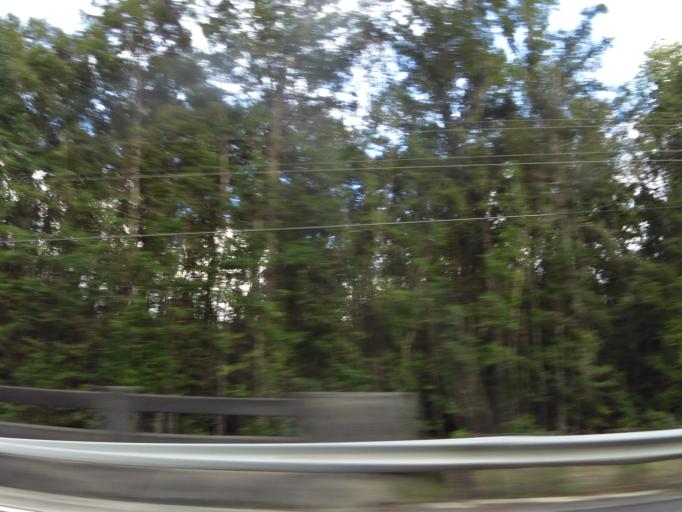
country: US
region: Georgia
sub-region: Liberty County
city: Midway
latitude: 31.8204
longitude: -81.4298
